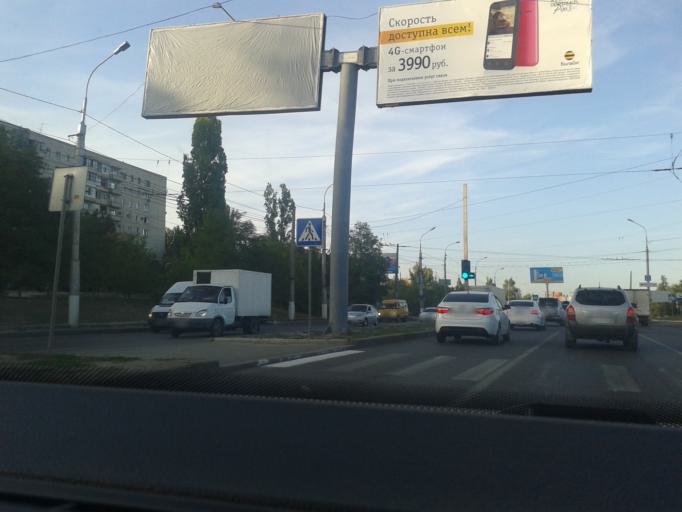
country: RU
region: Volgograd
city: Volgograd
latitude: 48.6459
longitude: 44.4336
